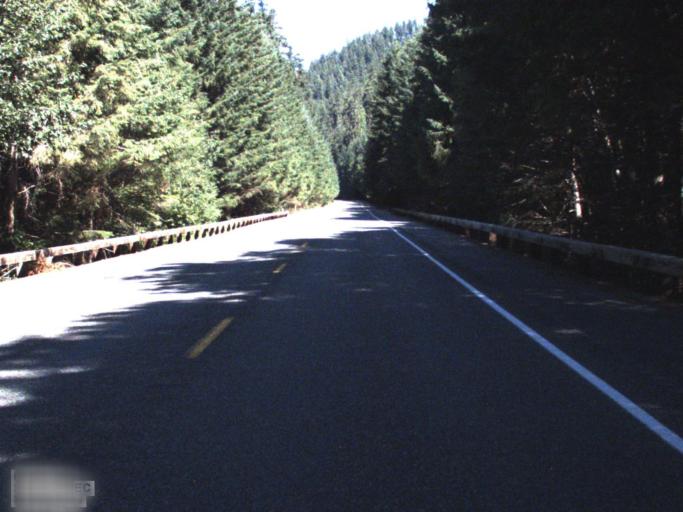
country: US
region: Washington
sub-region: King County
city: Riverbend
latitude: 47.0962
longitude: -121.5876
